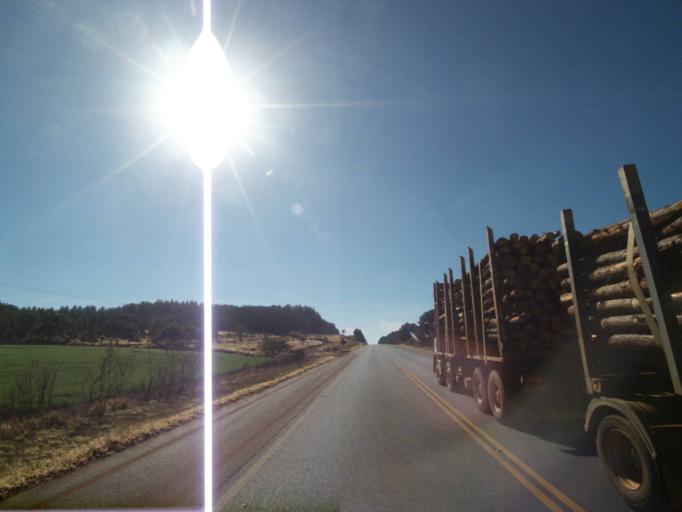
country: BR
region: Parana
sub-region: Tibagi
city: Tibagi
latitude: -24.4364
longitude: -50.4201
